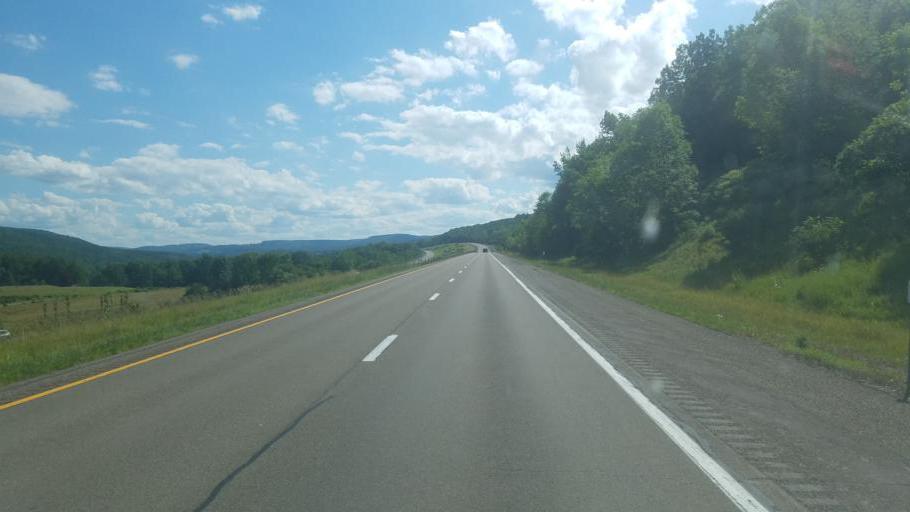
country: US
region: New York
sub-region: Steuben County
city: Hornell
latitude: 42.3580
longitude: -77.7092
